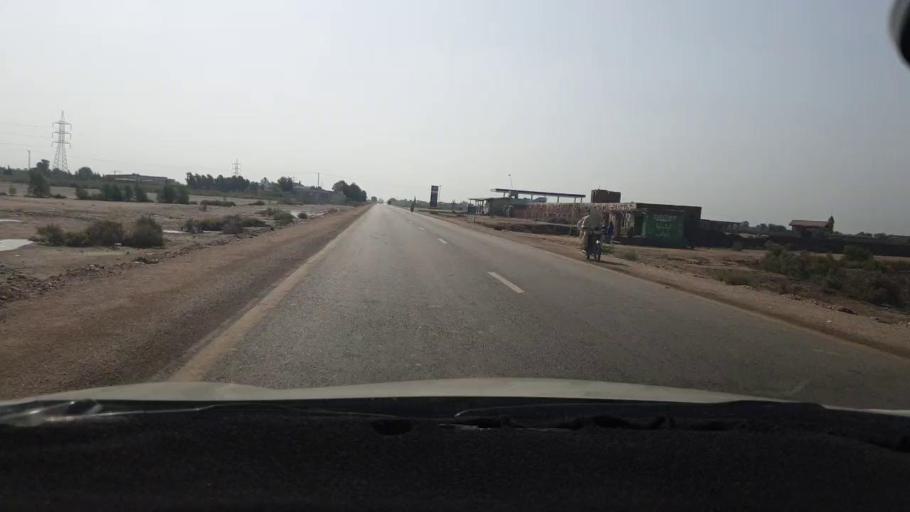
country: PK
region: Sindh
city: Jhol
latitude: 25.9228
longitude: 69.0024
